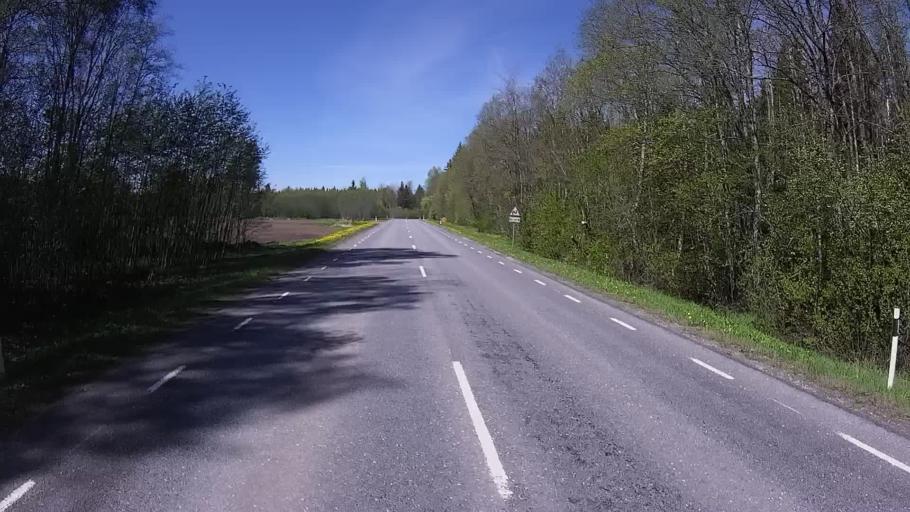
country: EE
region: Raplamaa
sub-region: Kehtna vald
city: Kehtna
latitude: 59.0445
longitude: 25.0276
